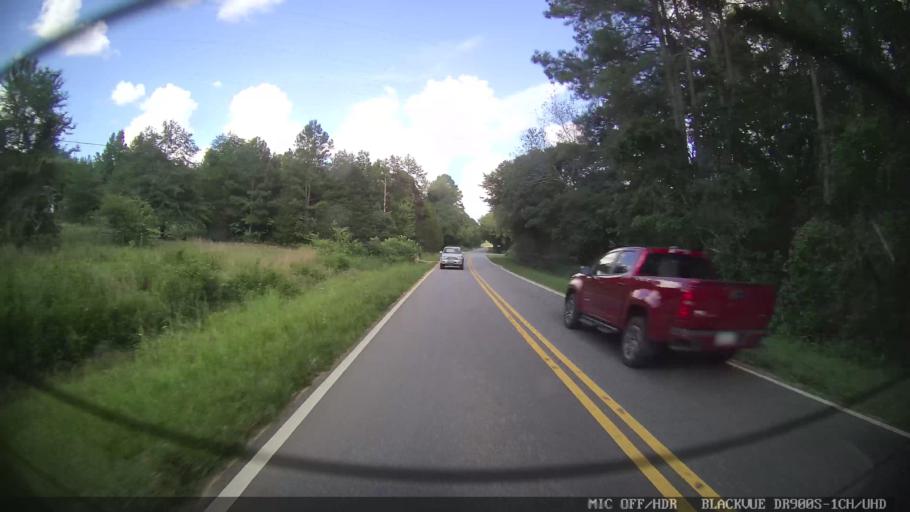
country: US
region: Georgia
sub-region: Bartow County
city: Euharlee
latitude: 34.1831
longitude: -85.0421
